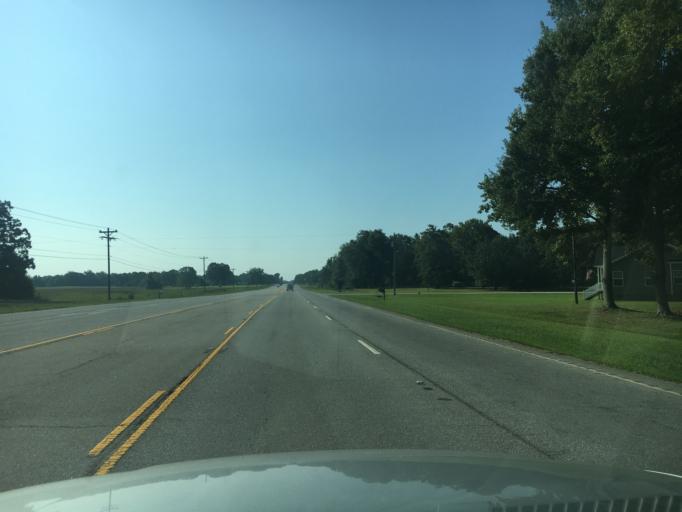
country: US
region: South Carolina
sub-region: Anderson County
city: Williamston
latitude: 34.5920
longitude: -82.3467
